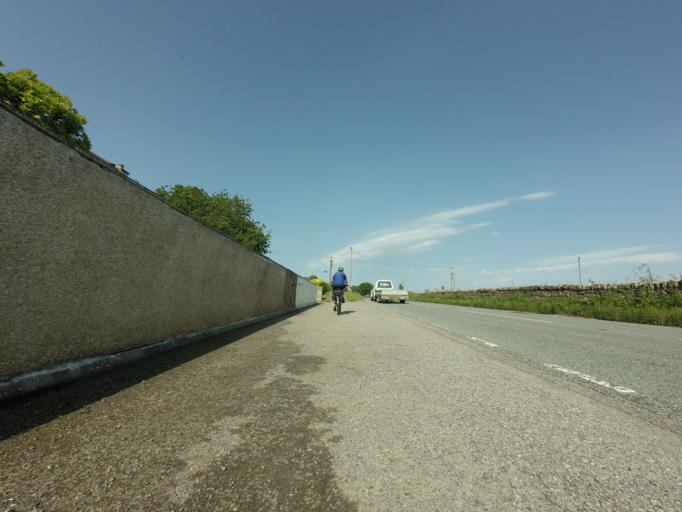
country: GB
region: Scotland
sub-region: Highland
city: Alness
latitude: 57.6883
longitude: -4.2803
